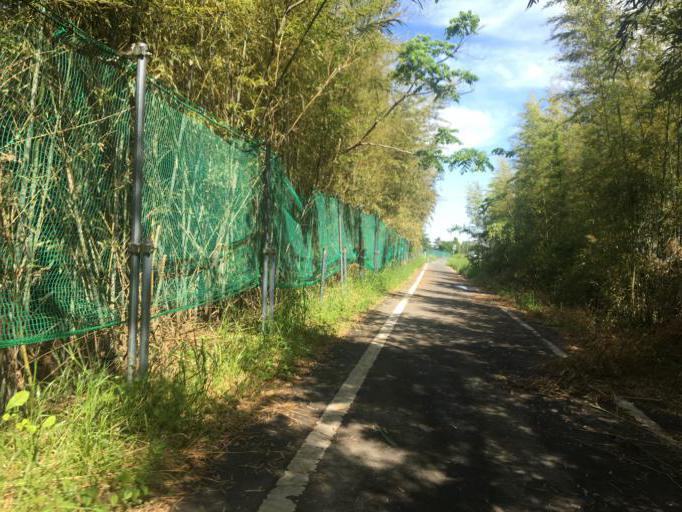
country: JP
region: Saitama
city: Shiki
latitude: 35.8649
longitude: 139.5837
